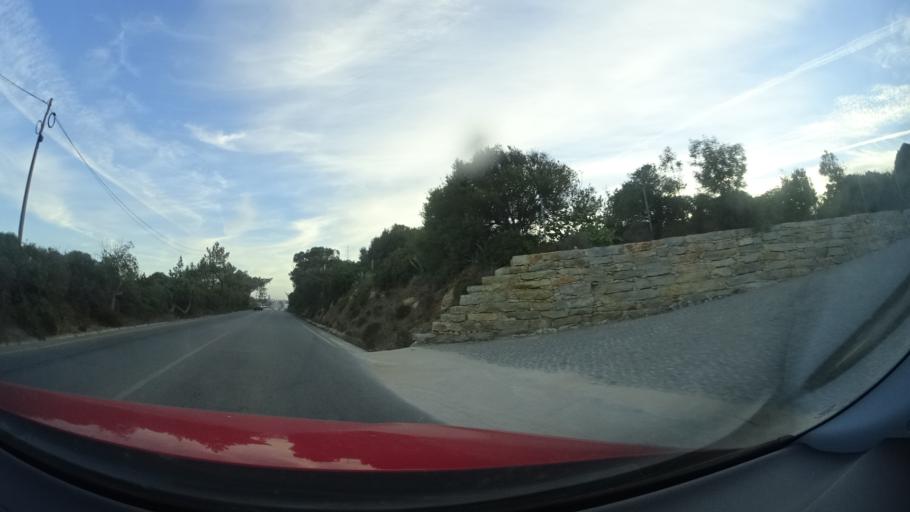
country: PT
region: Faro
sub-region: Vila do Bispo
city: Sagres
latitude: 37.0216
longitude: -8.9386
